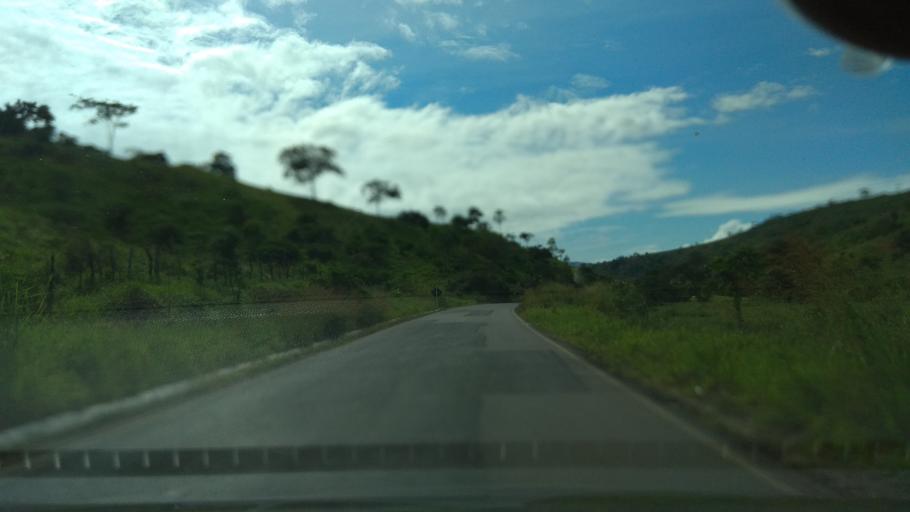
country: BR
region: Bahia
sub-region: Ubaira
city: Ubaira
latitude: -13.2642
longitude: -39.6861
